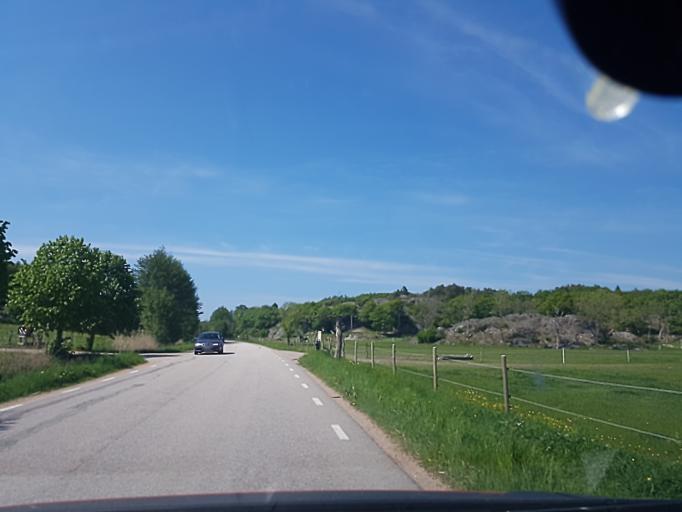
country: SE
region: Vaestra Goetaland
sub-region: Lysekils Kommun
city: Lysekil
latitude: 58.1614
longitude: 11.4548
